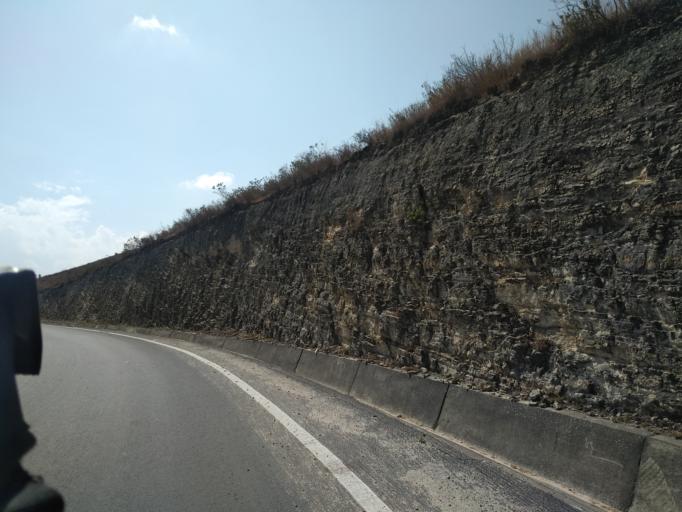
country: PE
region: Cajamarca
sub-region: Provincia de Cajamarca
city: Llacanora
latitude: -7.2069
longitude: -78.3900
